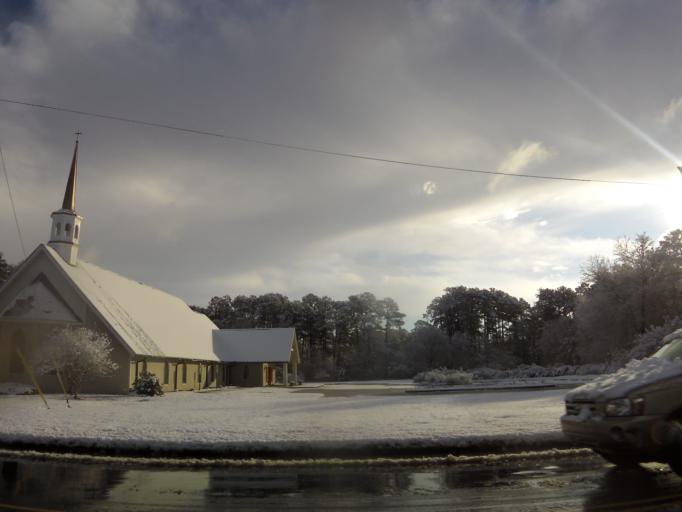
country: US
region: North Carolina
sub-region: Nash County
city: Rocky Mount
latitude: 35.9588
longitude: -77.8489
